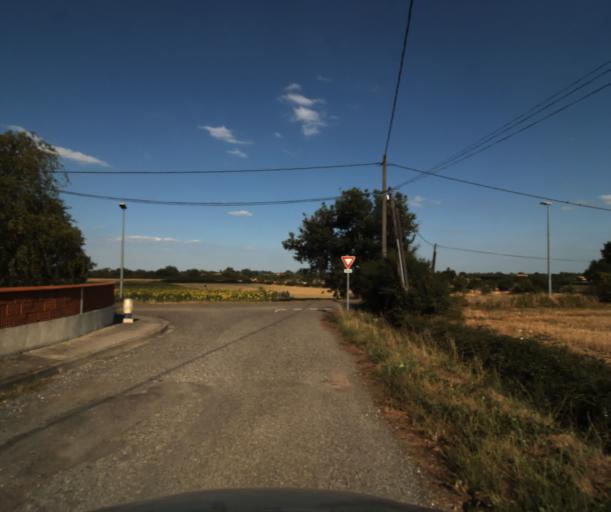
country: FR
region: Midi-Pyrenees
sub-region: Departement de la Haute-Garonne
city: Saint-Lys
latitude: 43.5062
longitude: 1.2001
